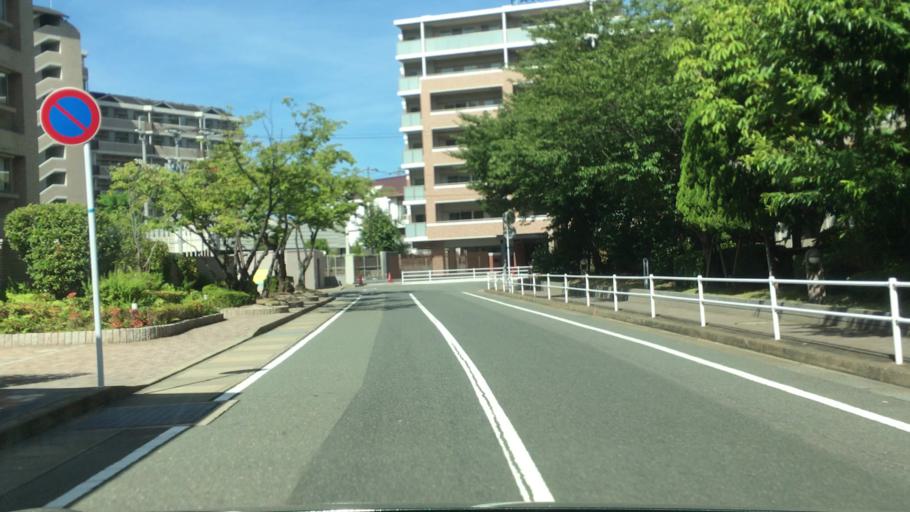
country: JP
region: Fukuoka
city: Fukuoka-shi
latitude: 33.5736
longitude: 130.3745
